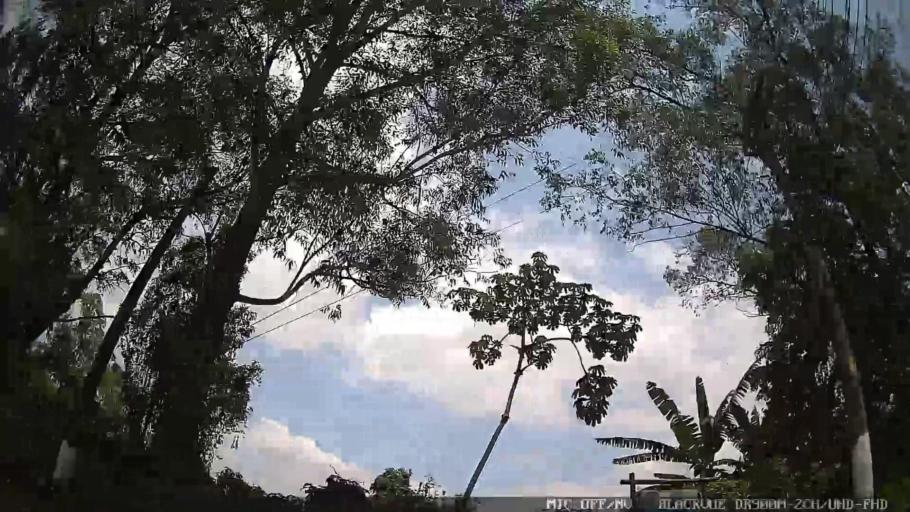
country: BR
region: Sao Paulo
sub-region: Caieiras
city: Caieiras
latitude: -23.4613
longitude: -46.7211
